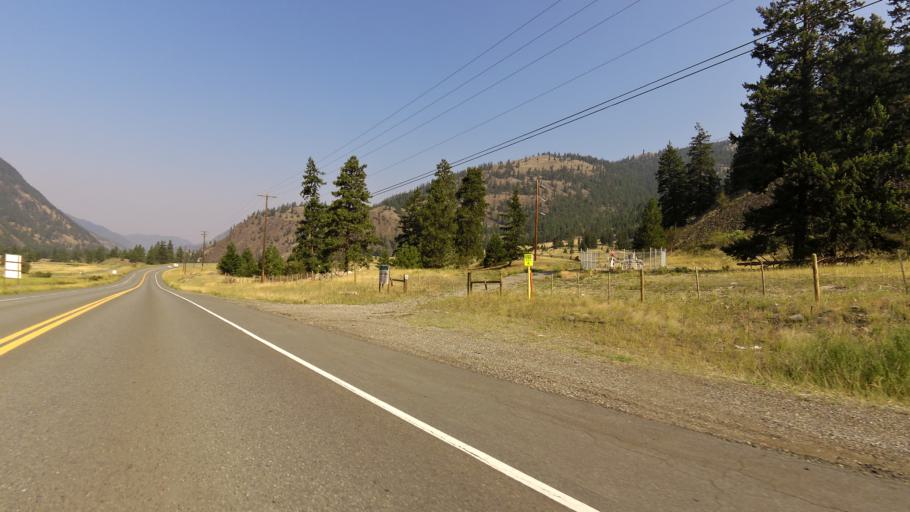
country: CA
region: British Columbia
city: Princeton
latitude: 49.3545
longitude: -120.0908
